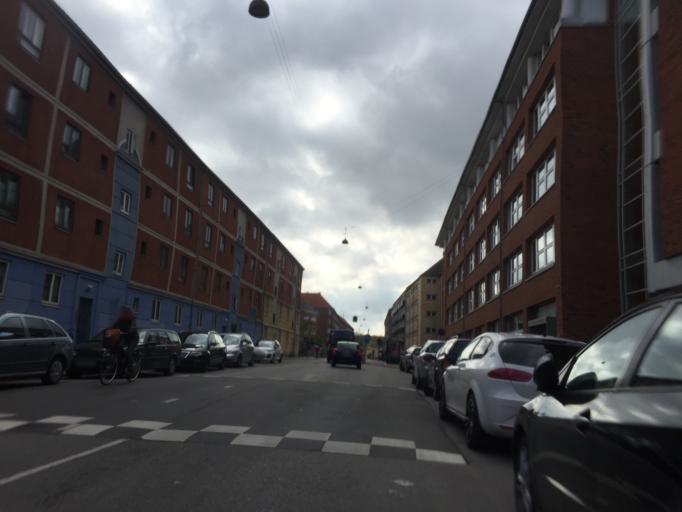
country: DK
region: Capital Region
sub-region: Frederiksberg Kommune
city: Frederiksberg
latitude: 55.6993
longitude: 12.5479
